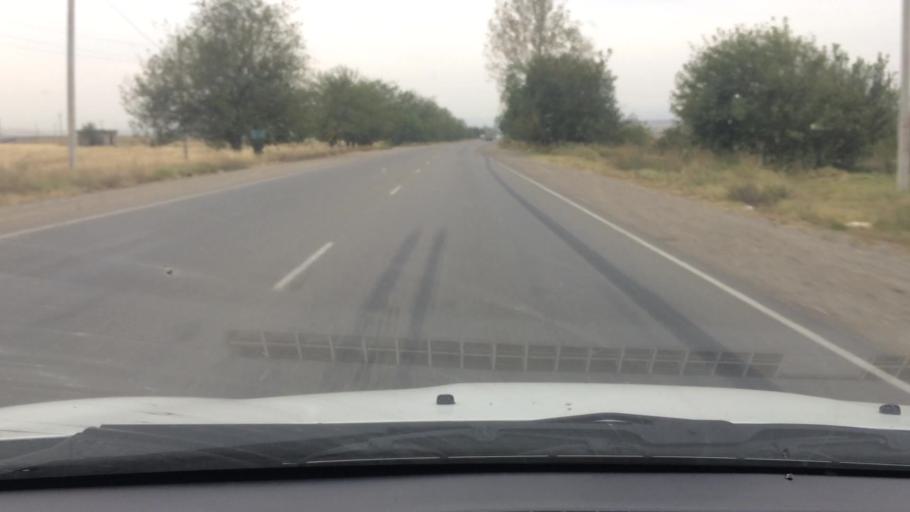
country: GE
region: Kvemo Kartli
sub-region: Marneuli
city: Marneuli
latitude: 41.5680
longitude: 44.7753
